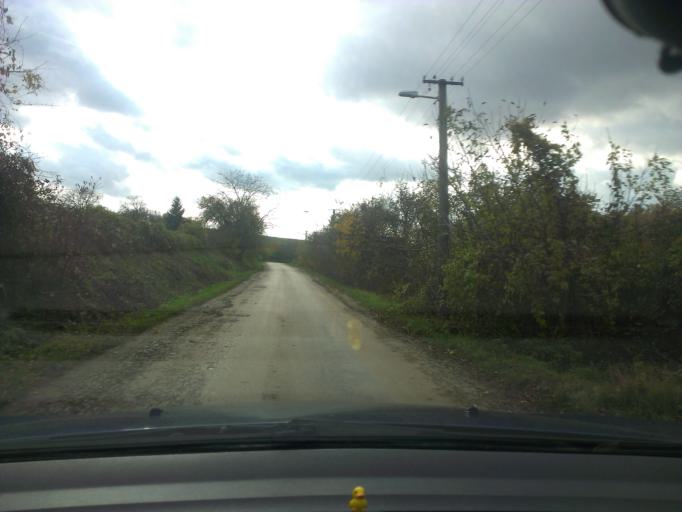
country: SK
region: Trnavsky
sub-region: Okres Trnava
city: Piestany
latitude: 48.6049
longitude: 17.8741
